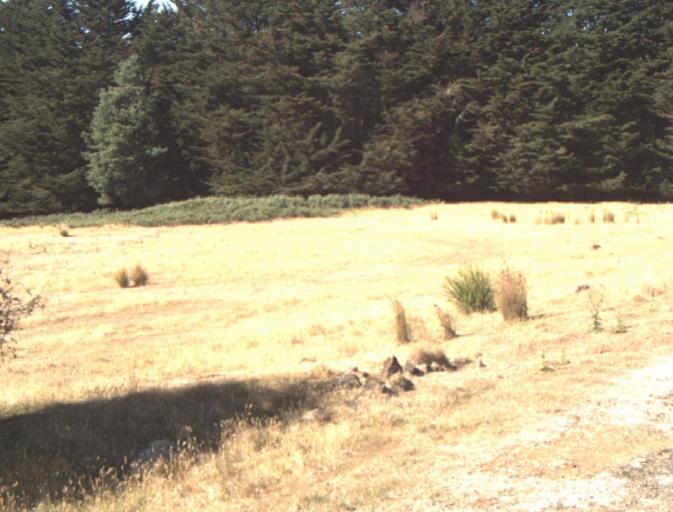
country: AU
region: Tasmania
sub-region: Dorset
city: Scottsdale
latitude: -41.2896
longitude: 147.3596
